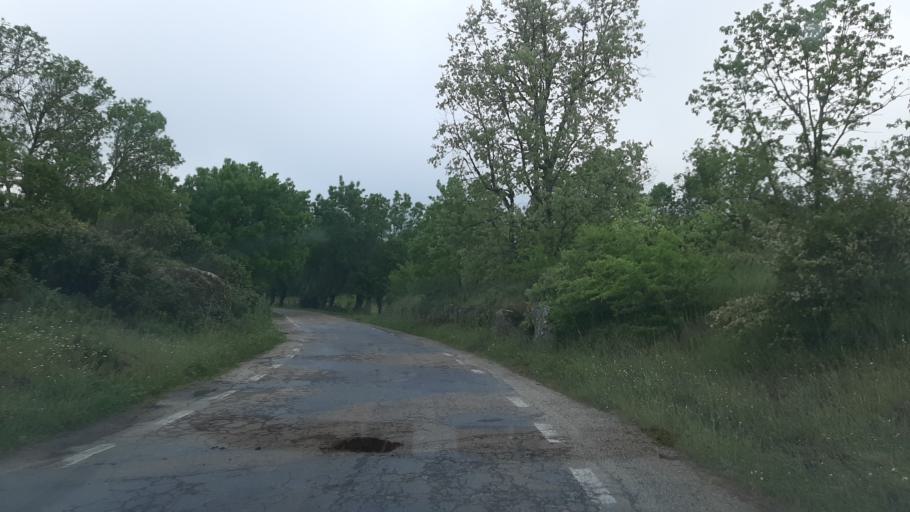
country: ES
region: Castille and Leon
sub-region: Provincia de Salamanca
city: Endrinal
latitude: 40.5501
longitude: -5.8021
